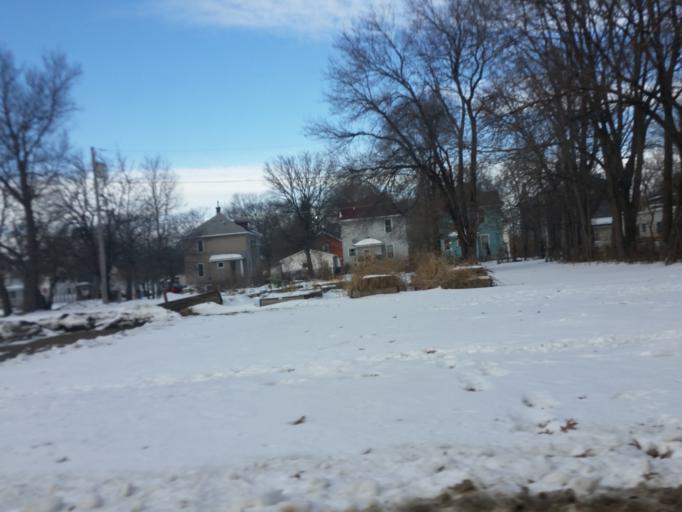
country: US
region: Iowa
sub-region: Black Hawk County
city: Waterloo
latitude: 42.5037
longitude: -92.3353
